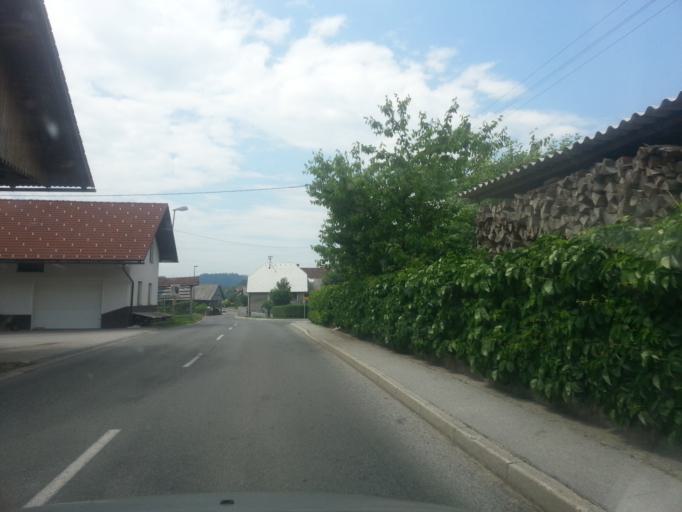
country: SI
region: Horjul
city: Horjul
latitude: 46.0239
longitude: 14.3155
